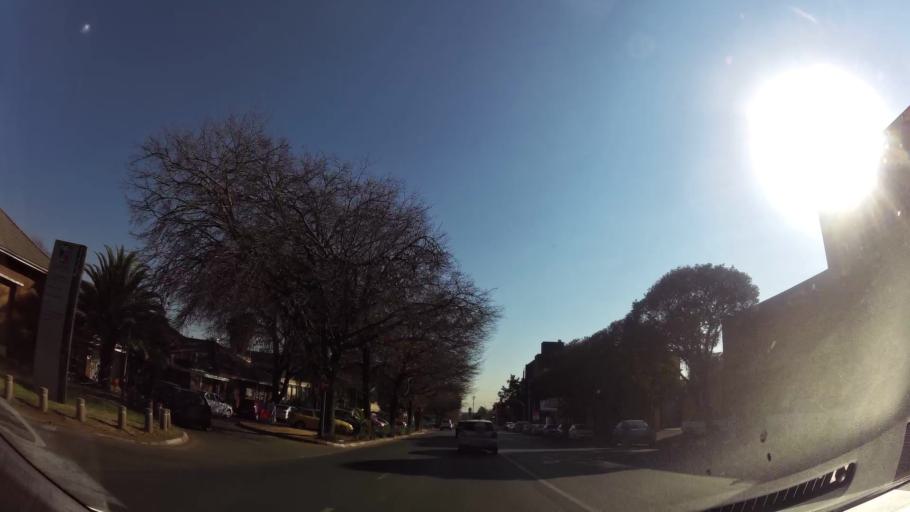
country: ZA
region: Gauteng
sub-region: Ekurhuleni Metropolitan Municipality
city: Germiston
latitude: -26.1794
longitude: 28.1361
